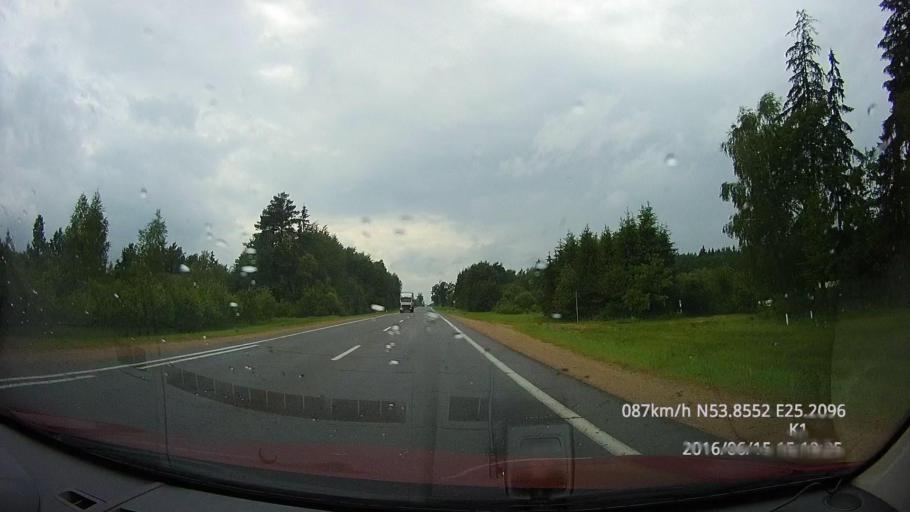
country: BY
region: Grodnenskaya
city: Lida
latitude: 53.8551
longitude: 25.2093
